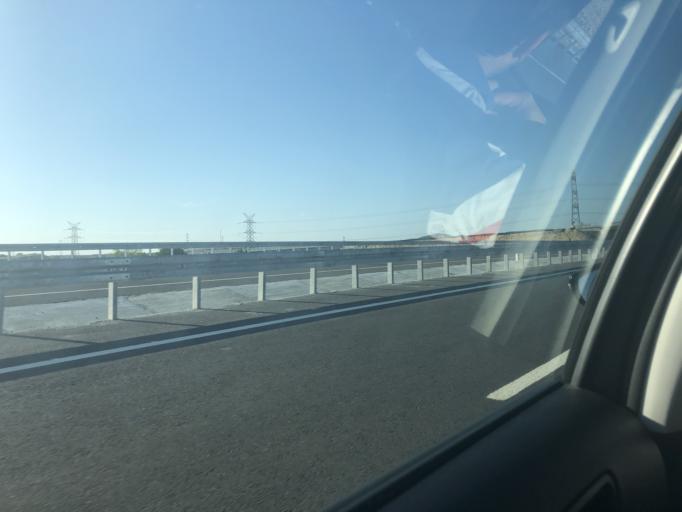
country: TR
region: Istanbul
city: Catalca
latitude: 41.1699
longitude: 28.4609
